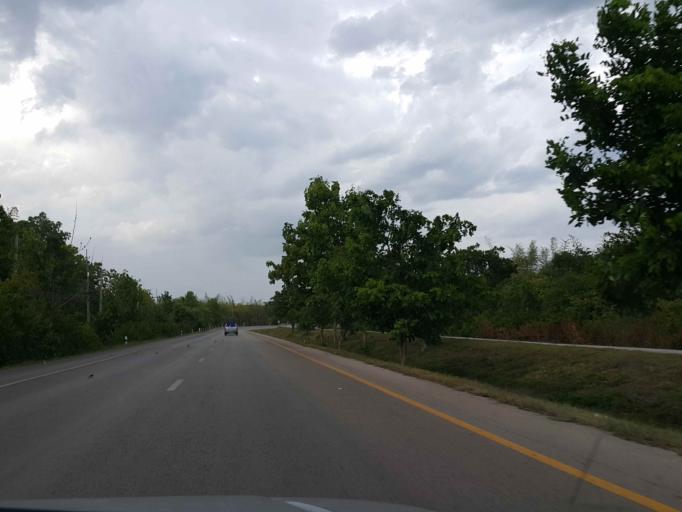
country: TH
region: Lampang
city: Sop Prap
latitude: 17.9651
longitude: 99.3533
